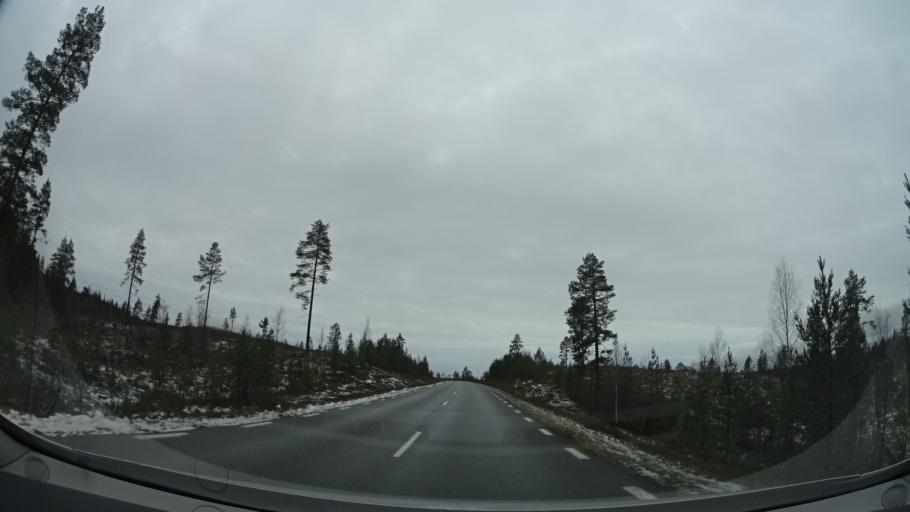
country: SE
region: Jaemtland
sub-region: Stroemsunds Kommun
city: Stroemsund
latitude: 63.9838
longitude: 15.4969
